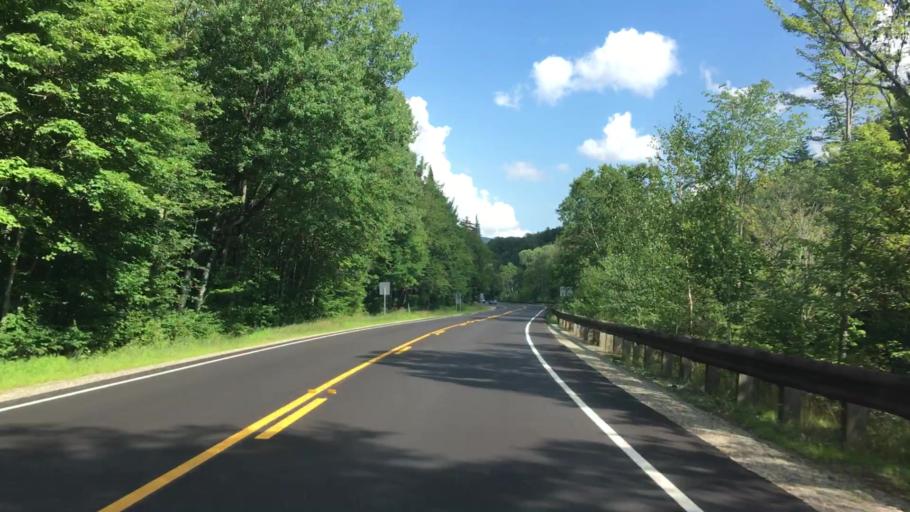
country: US
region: New Hampshire
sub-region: Grafton County
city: North Haverhill
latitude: 44.0990
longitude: -71.8508
